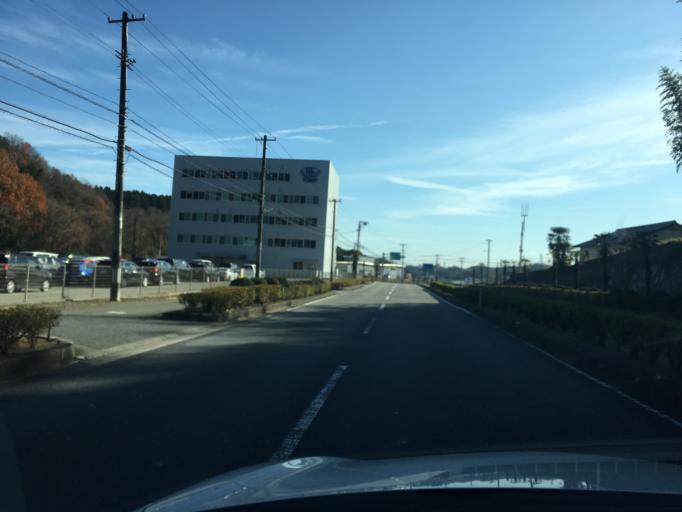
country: JP
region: Fukushima
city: Iwaki
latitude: 36.9989
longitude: 140.8221
